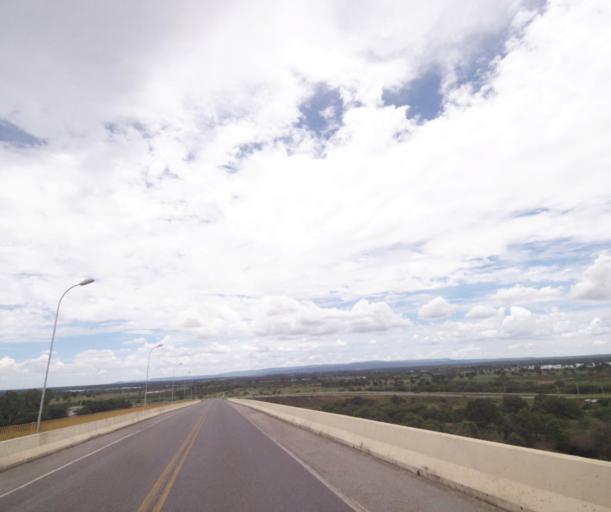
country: BR
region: Bahia
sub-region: Carinhanha
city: Carinhanha
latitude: -14.3262
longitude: -43.7674
